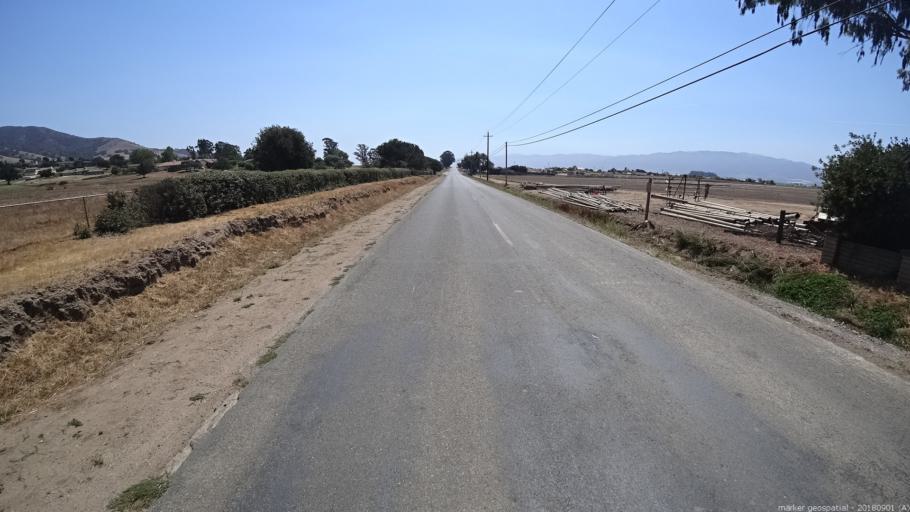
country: US
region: California
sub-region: Monterey County
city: Salinas
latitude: 36.6717
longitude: -121.5528
